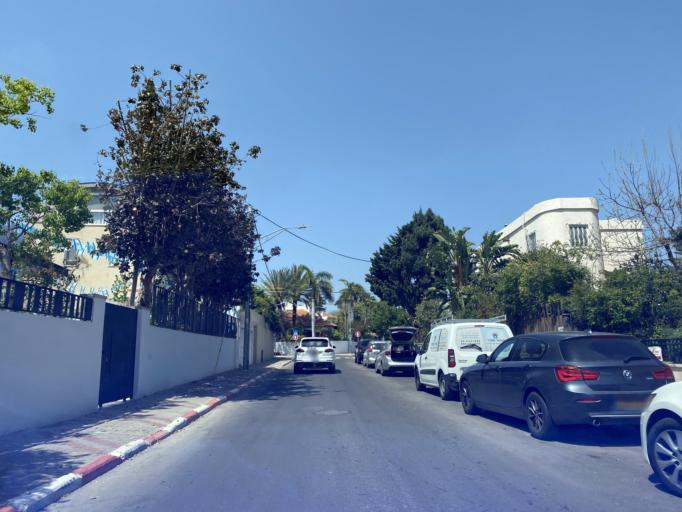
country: IL
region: Tel Aviv
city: Herzliya Pituah
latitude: 32.1725
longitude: 34.8107
